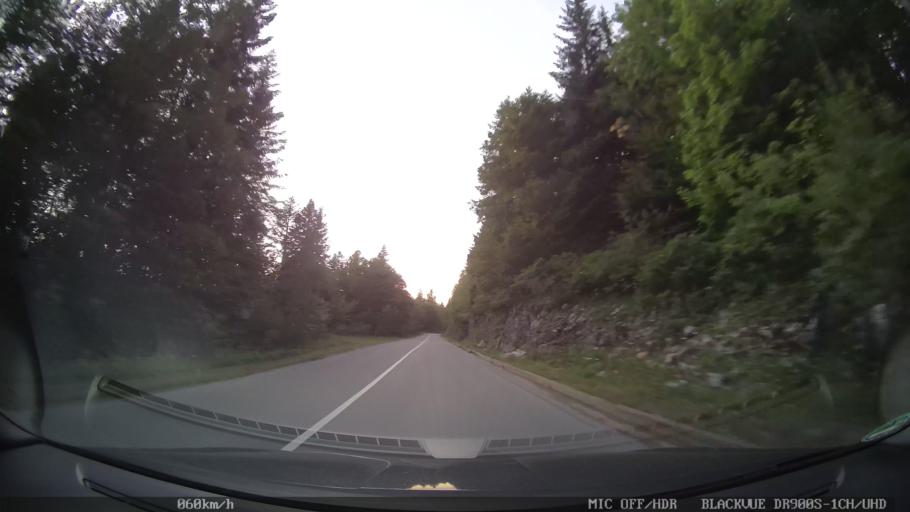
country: HR
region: Primorsko-Goranska
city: Novi Vinodolski
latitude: 45.1817
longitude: 14.9283
